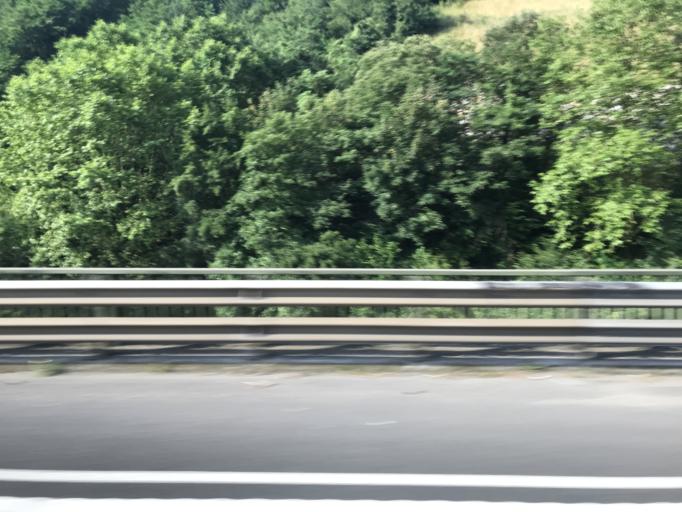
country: ES
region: Basque Country
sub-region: Provincia de Guipuzcoa
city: Beasain
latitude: 43.0460
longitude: -2.2069
